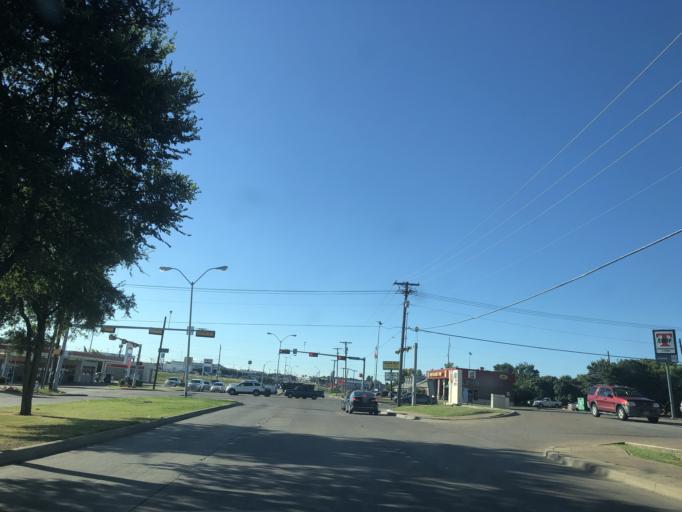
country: US
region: Texas
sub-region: Dallas County
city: Mesquite
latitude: 32.8343
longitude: -96.6346
